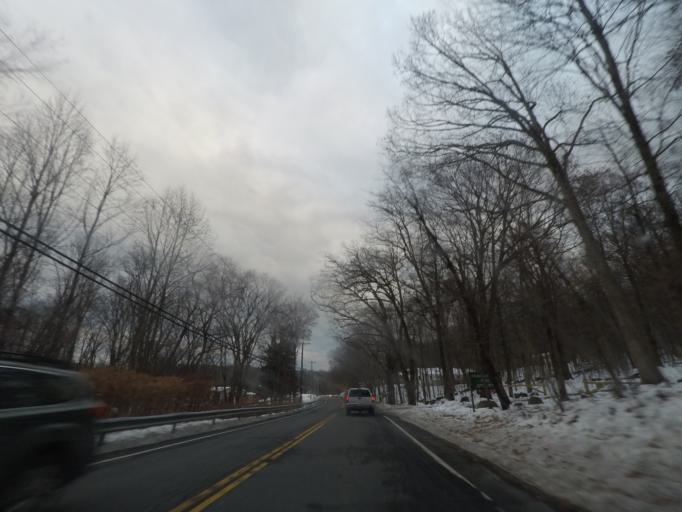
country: US
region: New York
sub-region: Orange County
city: Gardnertown
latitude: 41.5416
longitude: -74.0453
